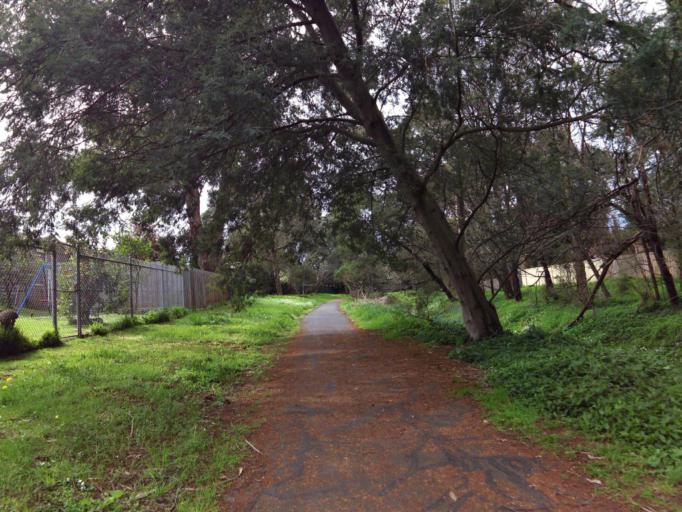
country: AU
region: Victoria
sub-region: Maroondah
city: Croydon Hills
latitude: -37.7934
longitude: 145.2552
